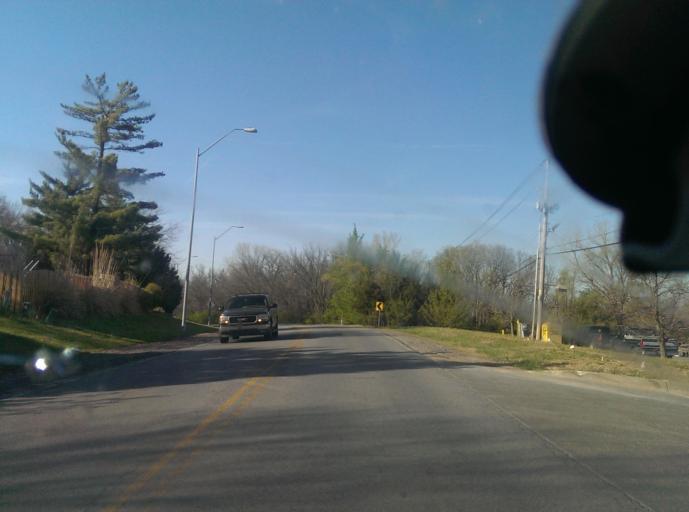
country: US
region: Missouri
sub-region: Jackson County
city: Grandview
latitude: 38.8909
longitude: -94.5859
